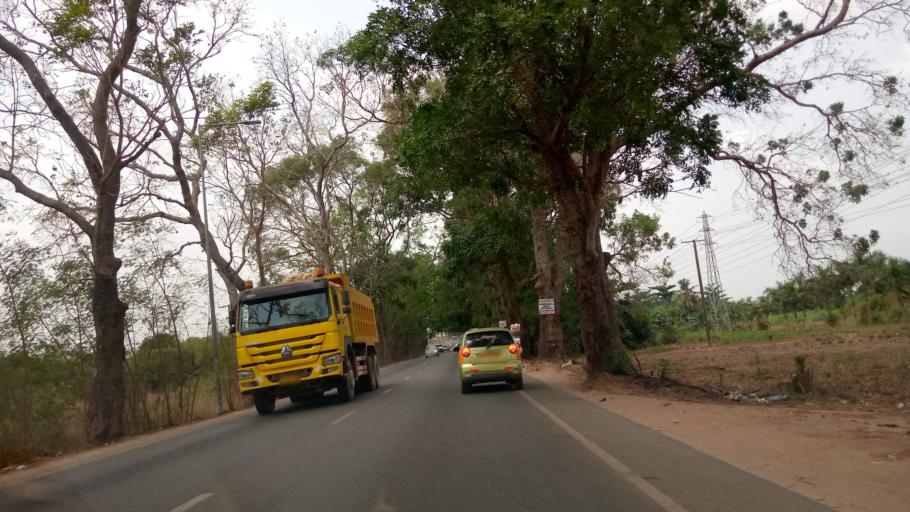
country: GH
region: Greater Accra
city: Dome
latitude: 5.6677
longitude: -0.2264
